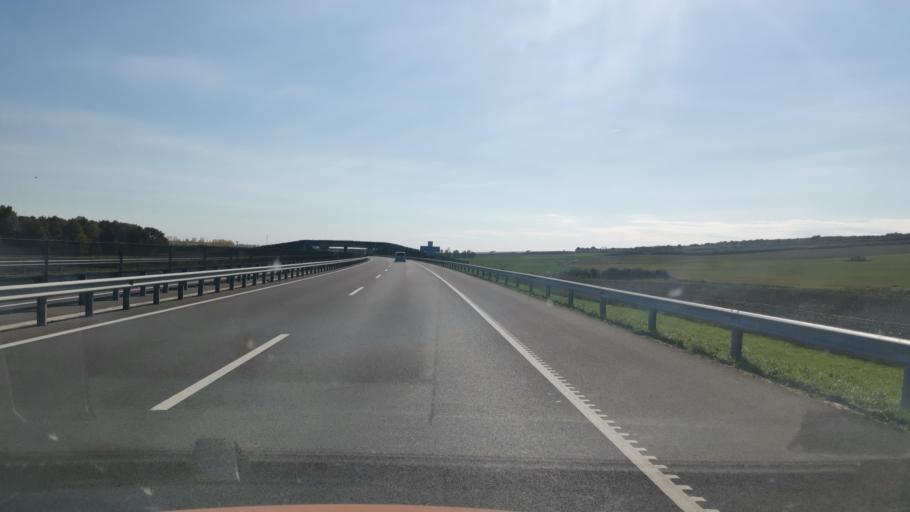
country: HU
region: Borsod-Abauj-Zemplen
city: Szikszo
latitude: 48.1918
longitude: 20.9063
